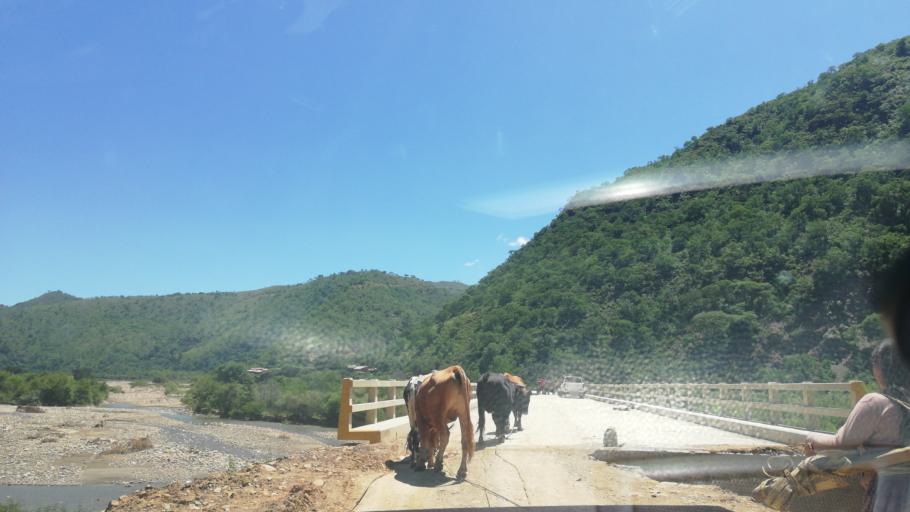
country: BO
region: Cochabamba
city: Mizque
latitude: -17.8194
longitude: -65.2947
